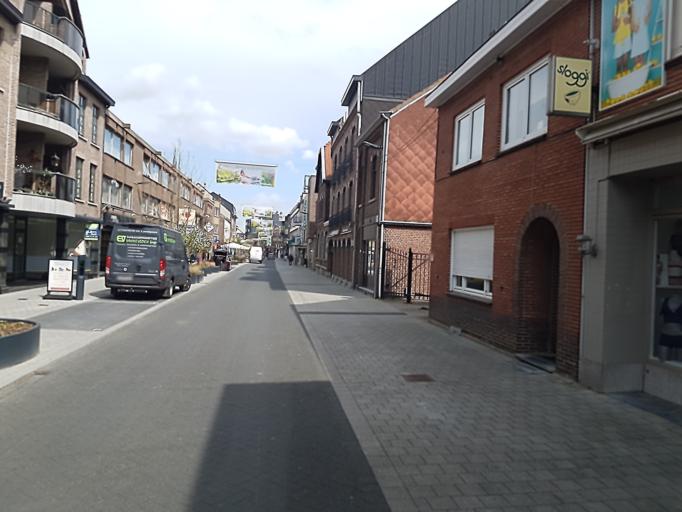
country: BE
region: Flanders
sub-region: Provincie Limburg
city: Lanaken
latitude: 50.8877
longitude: 5.6486
